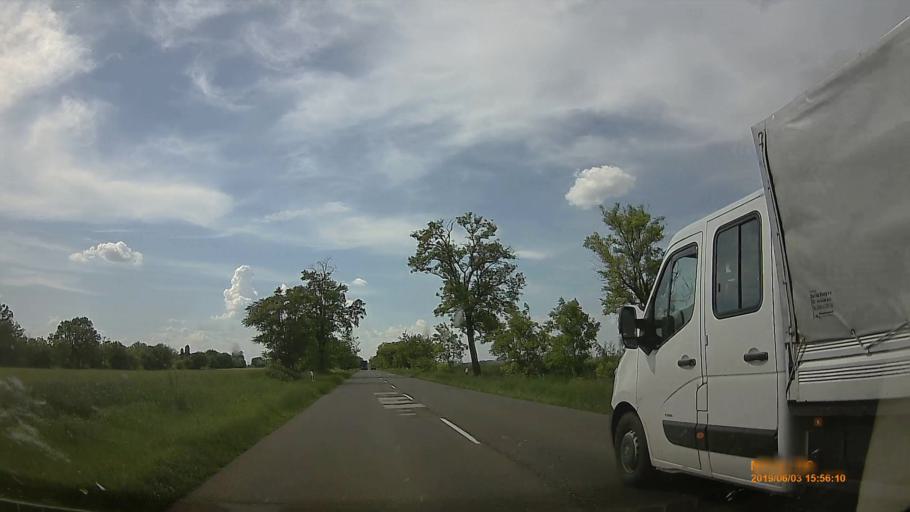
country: HU
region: Bacs-Kiskun
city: Harta
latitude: 46.7581
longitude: 19.1001
